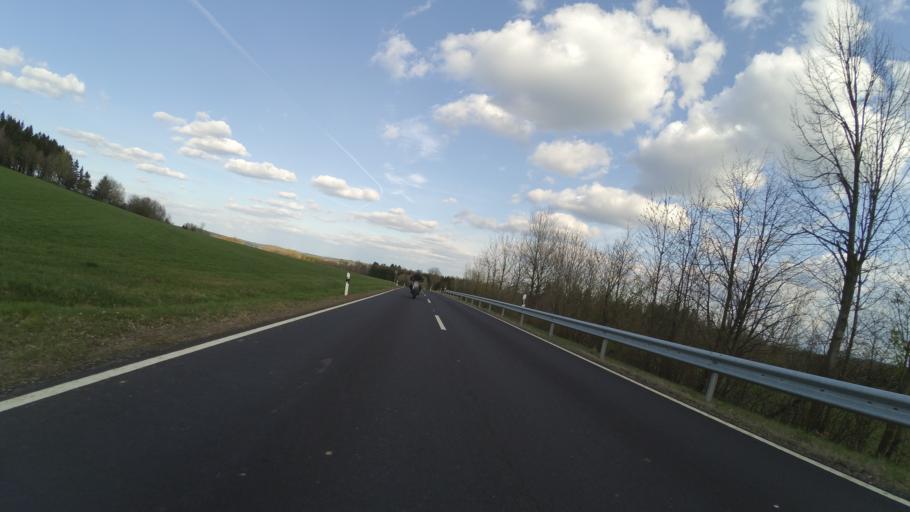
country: DE
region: Rheinland-Pfalz
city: Sarmersbach
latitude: 50.2391
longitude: 6.8980
